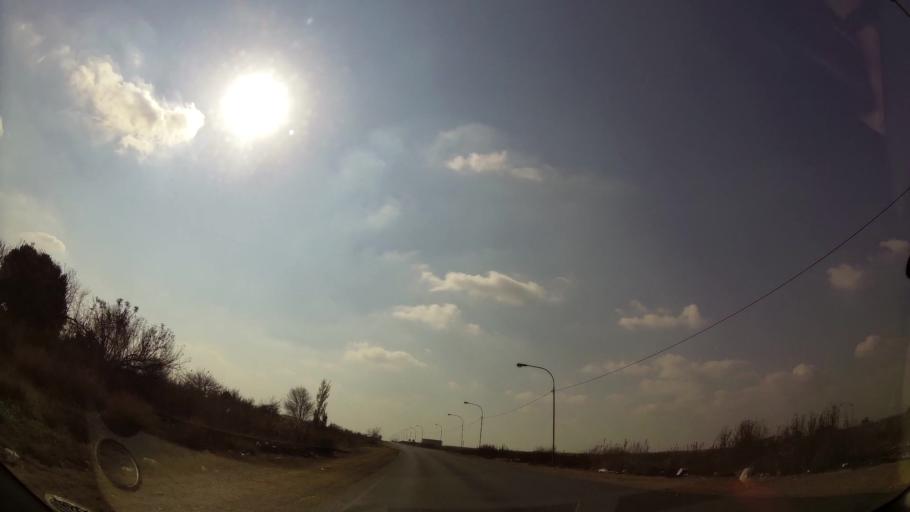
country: ZA
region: Gauteng
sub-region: Ekurhuleni Metropolitan Municipality
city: Springs
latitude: -26.1314
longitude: 28.4838
